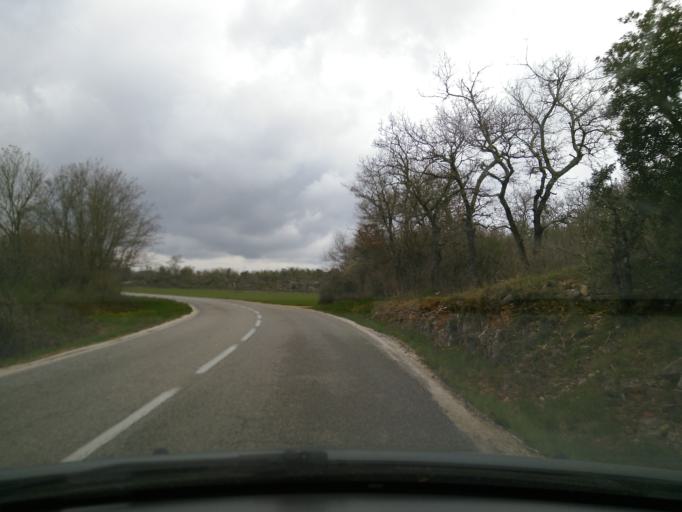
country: FR
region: Languedoc-Roussillon
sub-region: Departement du Gard
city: Barjac
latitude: 44.3578
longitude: 4.3758
